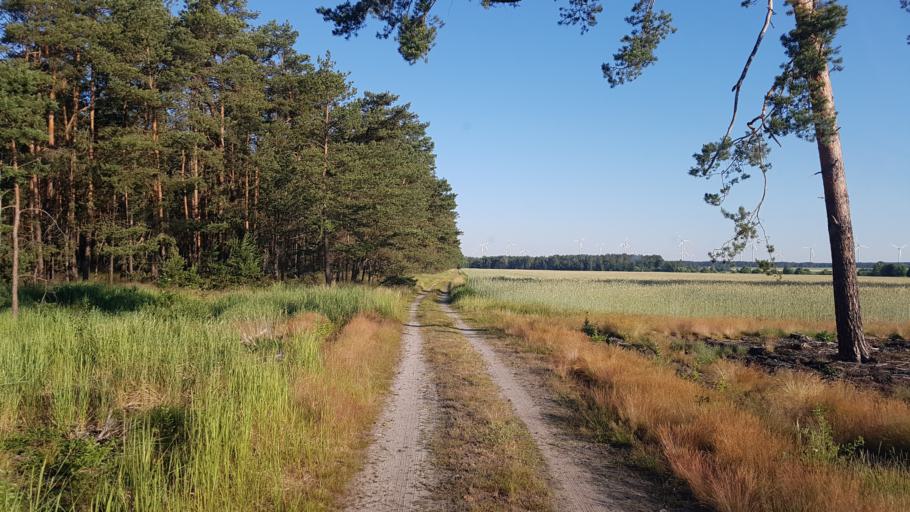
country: DE
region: Brandenburg
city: Trobitz
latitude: 51.6334
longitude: 13.4087
